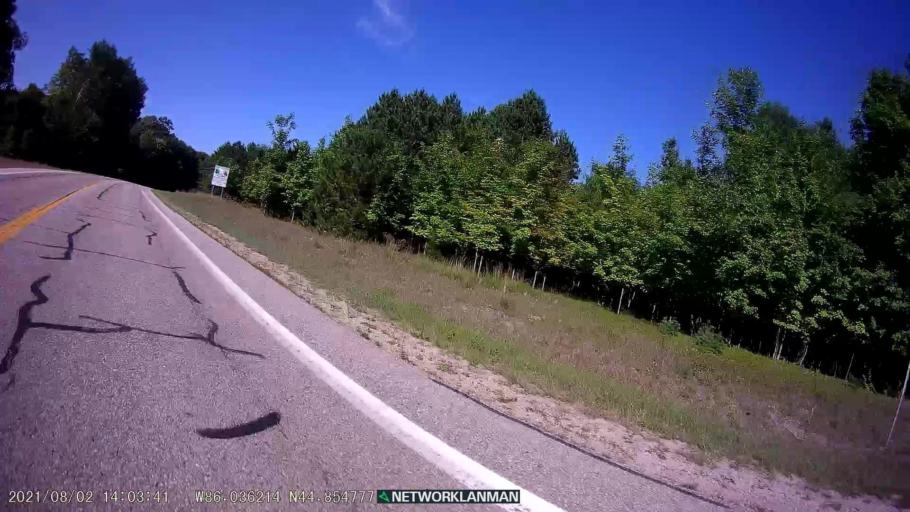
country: US
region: Michigan
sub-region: Benzie County
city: Beulah
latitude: 44.8553
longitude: -86.0362
